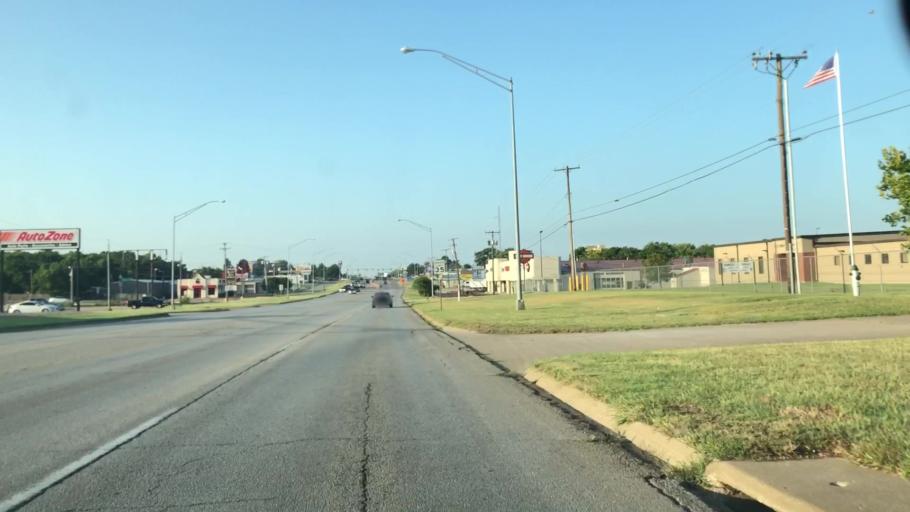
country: US
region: Oklahoma
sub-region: Washington County
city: Dewey
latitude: 36.7614
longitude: -95.9355
